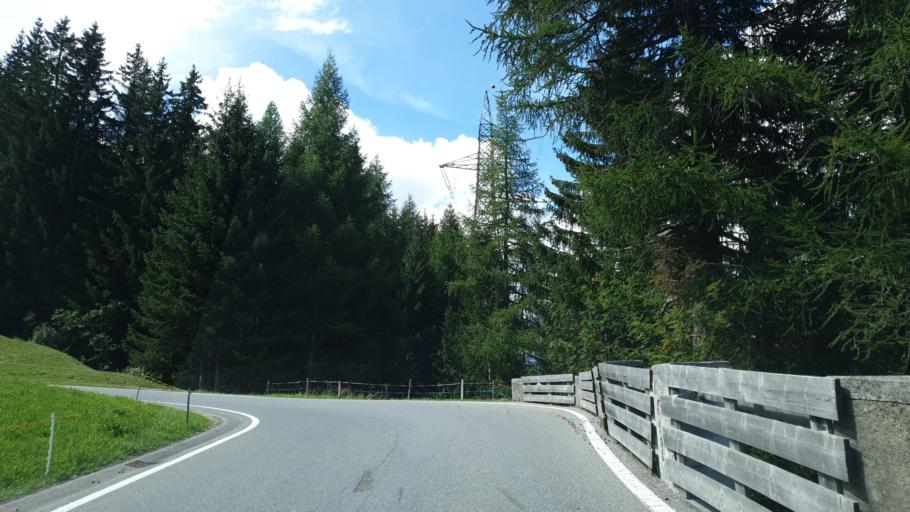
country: CH
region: Grisons
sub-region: Hinterrhein District
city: Hinterrhein
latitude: 46.5459
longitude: 9.3207
